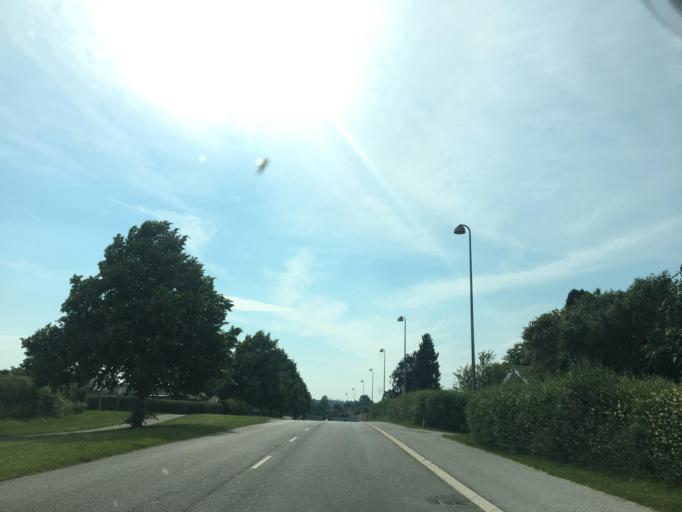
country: DK
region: Zealand
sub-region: Greve Kommune
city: Tune
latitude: 55.5969
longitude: 12.2022
